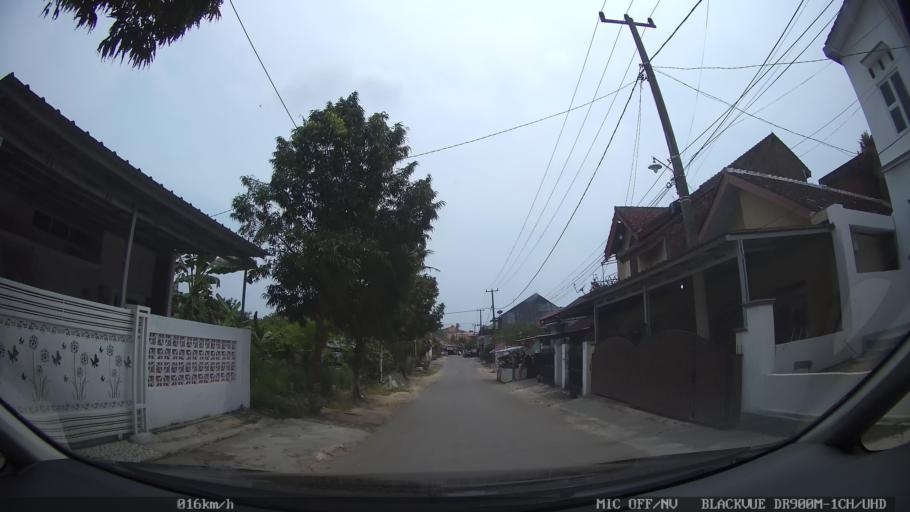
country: ID
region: Lampung
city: Kedaton
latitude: -5.4027
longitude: 105.3218
